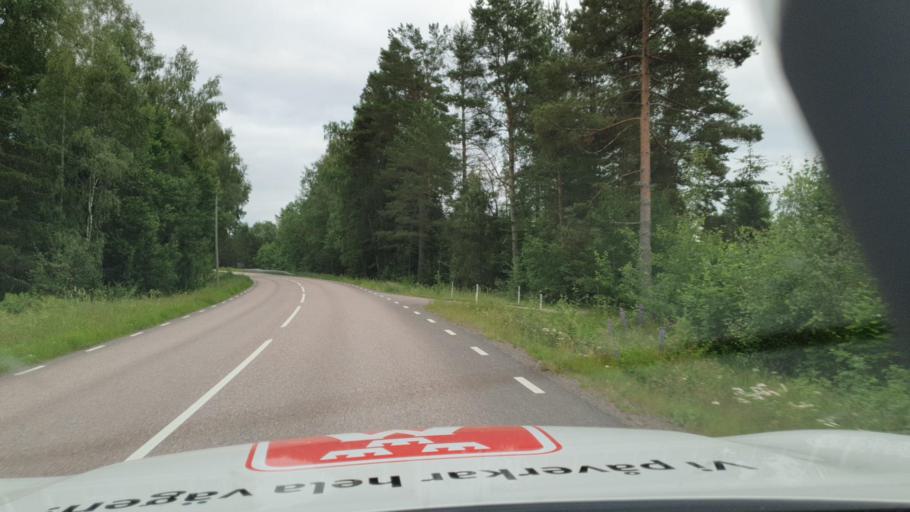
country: SE
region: Vaermland
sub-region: Kils Kommun
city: Kil
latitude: 59.5043
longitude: 13.3931
